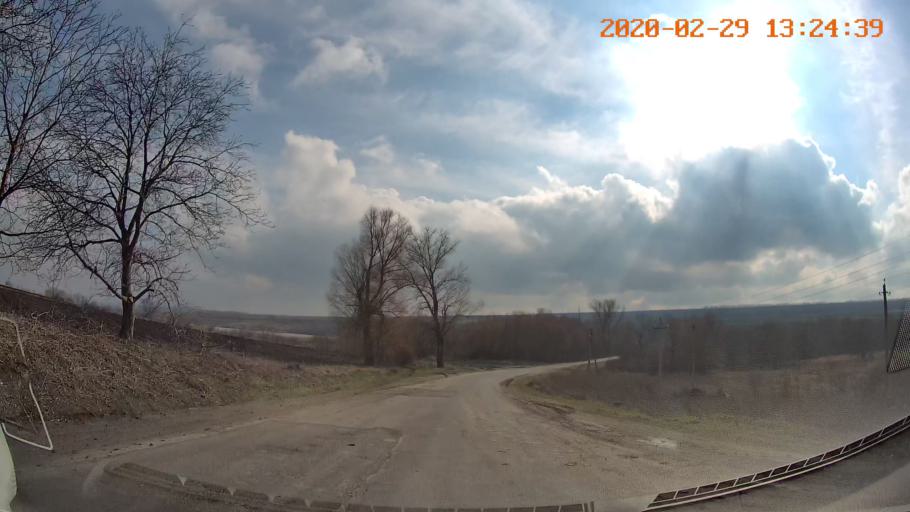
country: MD
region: Telenesti
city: Camenca
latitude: 47.9367
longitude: 28.6285
